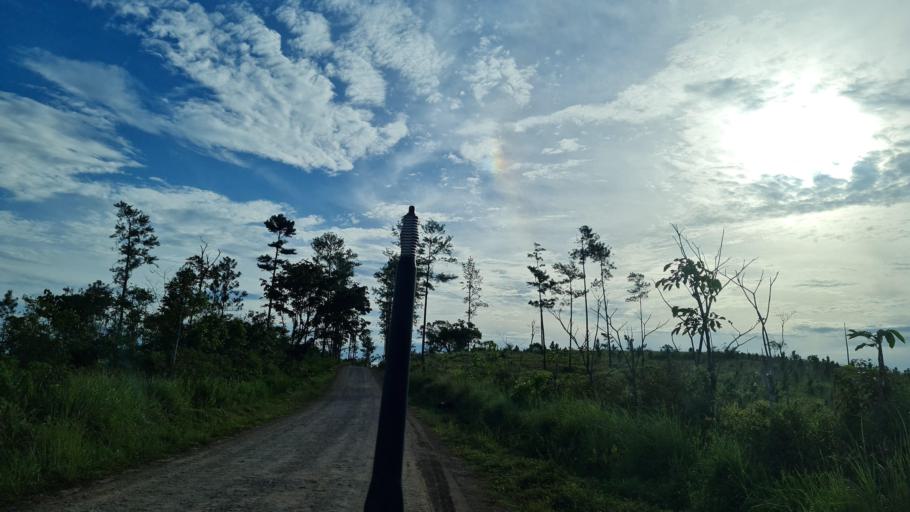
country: NI
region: Atlantico Sur
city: La Cruz de Rio Grande
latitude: 13.5562
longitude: -84.2983
